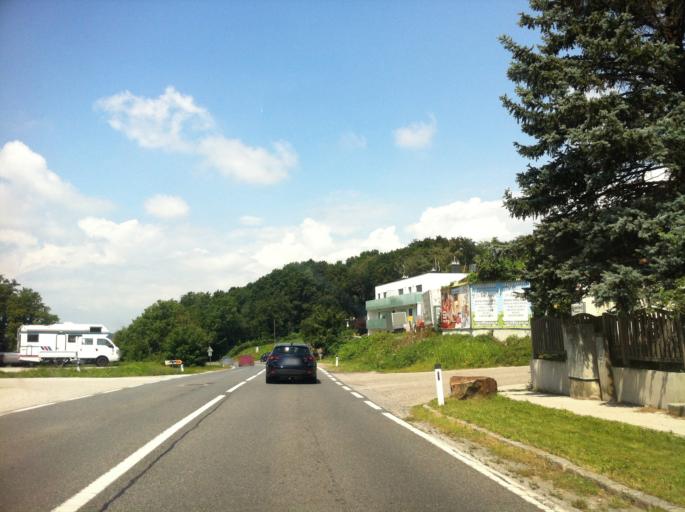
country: AT
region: Lower Austria
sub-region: Politischer Bezirk Tulln
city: Tulbing
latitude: 48.2500
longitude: 16.0947
